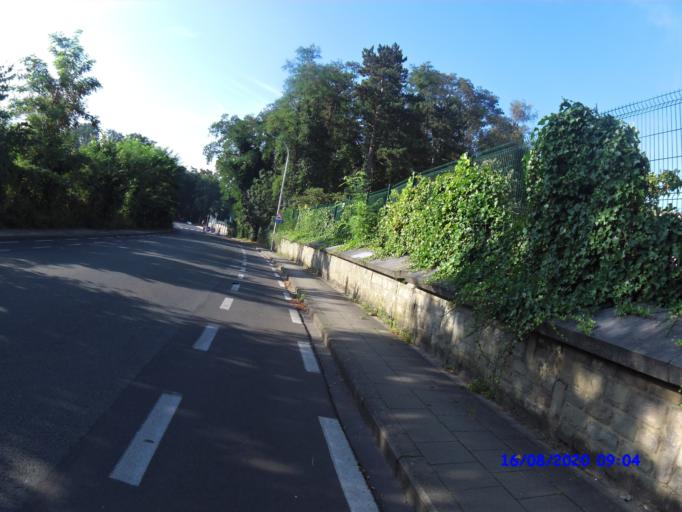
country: BE
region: Flanders
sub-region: Provincie Vlaams-Brabant
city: Linkebeek
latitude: 50.7800
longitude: 4.3321
